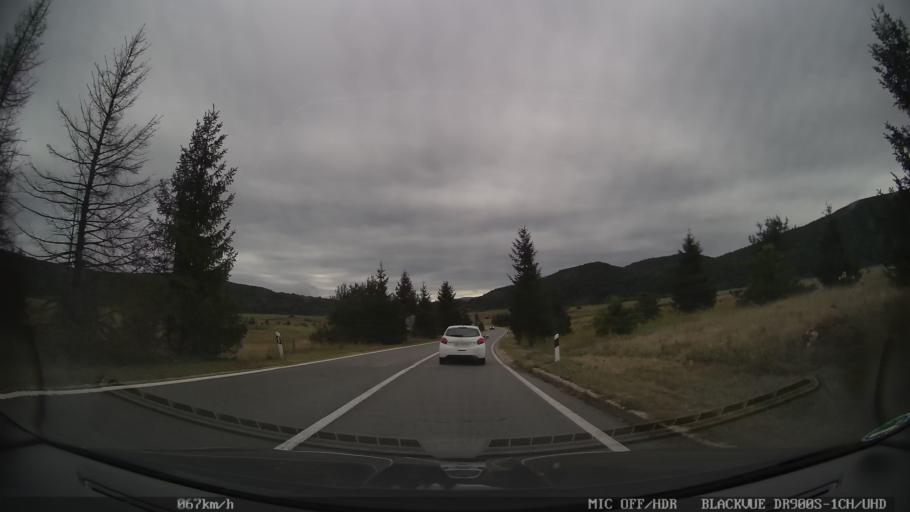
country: HR
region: Licko-Senjska
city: Jezerce
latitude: 44.7967
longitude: 15.5737
